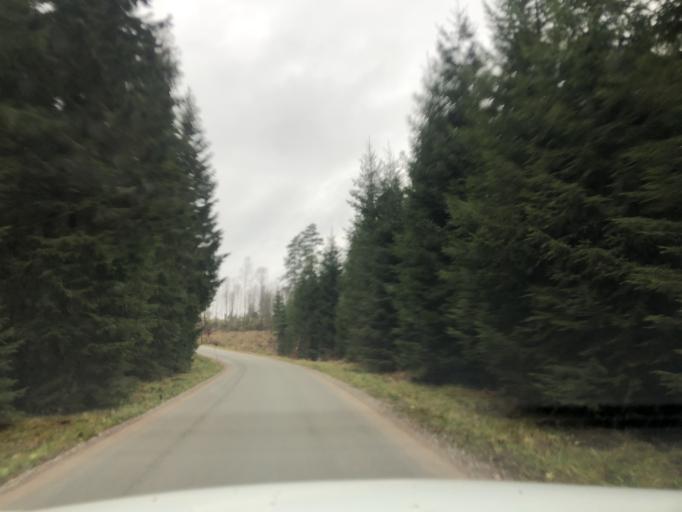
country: SE
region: Vaestra Goetaland
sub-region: Ulricehamns Kommun
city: Ulricehamn
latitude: 57.8583
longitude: 13.6178
